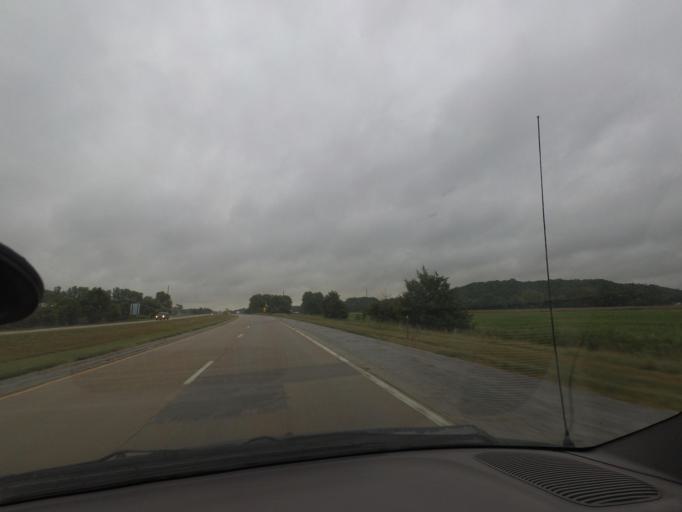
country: US
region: Illinois
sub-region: Adams County
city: Payson
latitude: 39.7187
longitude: -91.1795
